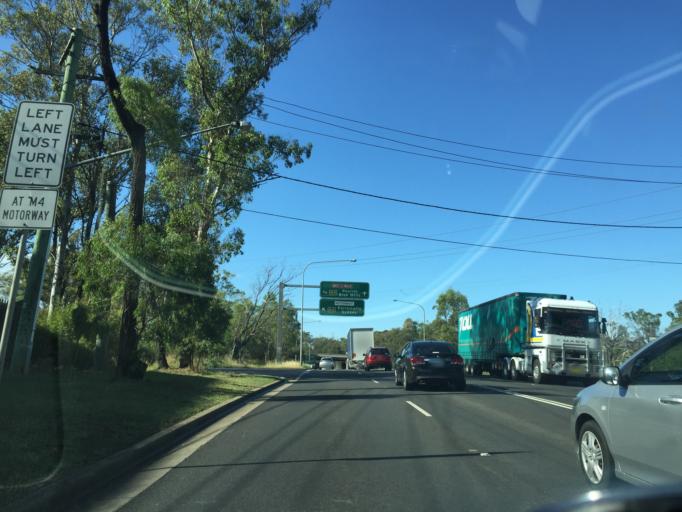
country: AU
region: New South Wales
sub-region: Blacktown
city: Blacktown
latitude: -33.8003
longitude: 150.8965
